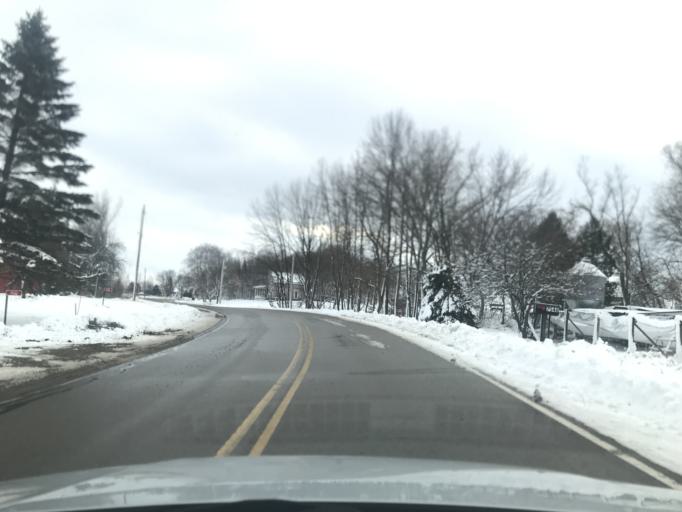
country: US
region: Wisconsin
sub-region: Oconto County
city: Oconto
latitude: 44.9448
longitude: -87.9875
